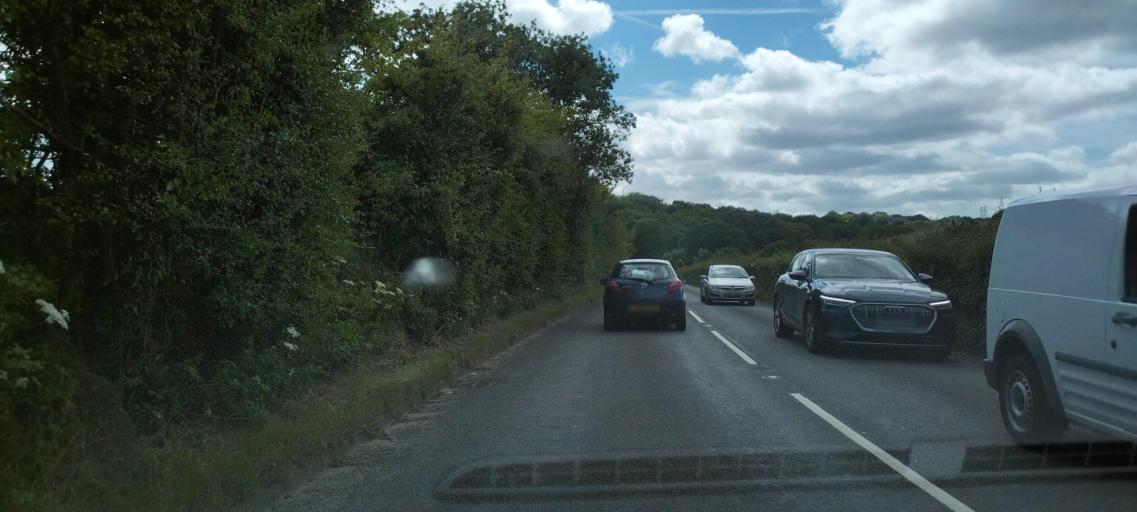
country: GB
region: England
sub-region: Blackburn with Darwen
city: Blackburn
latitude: 53.7207
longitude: -2.5554
